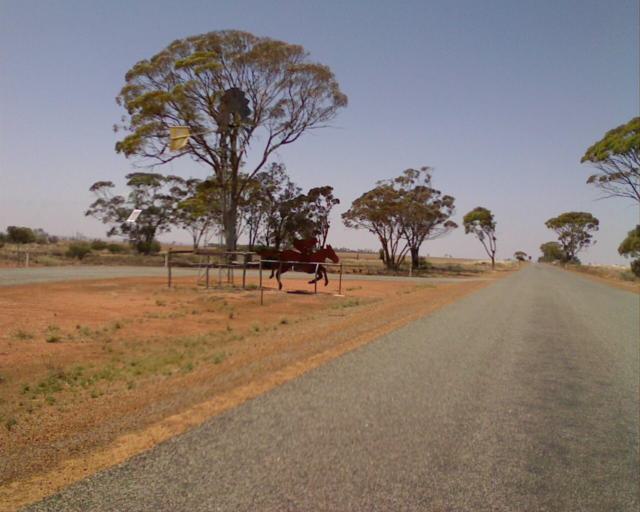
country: AU
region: Western Australia
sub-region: Merredin
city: Merredin
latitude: -30.8124
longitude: 118.2094
